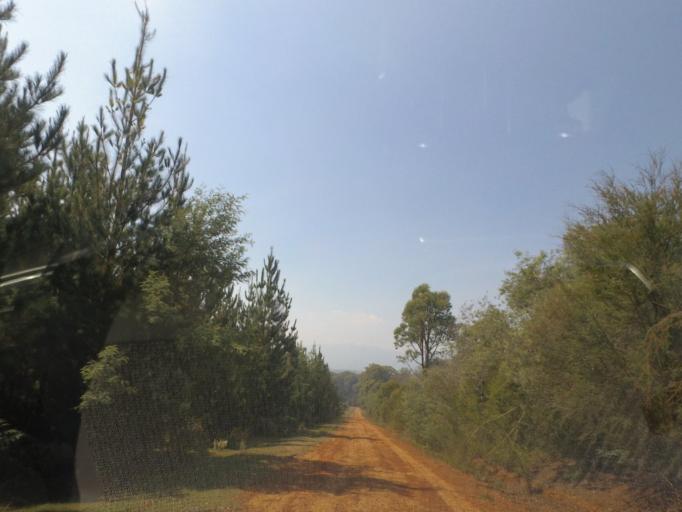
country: AU
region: Victoria
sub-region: Yarra Ranges
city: Healesville
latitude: -37.5596
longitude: 145.6389
